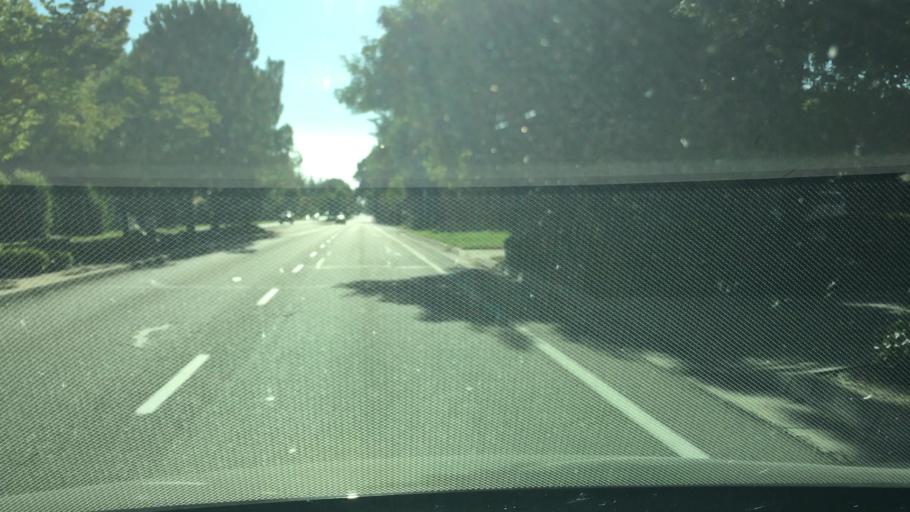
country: US
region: California
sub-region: Fresno County
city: Clovis
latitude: 36.8663
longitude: -119.7765
